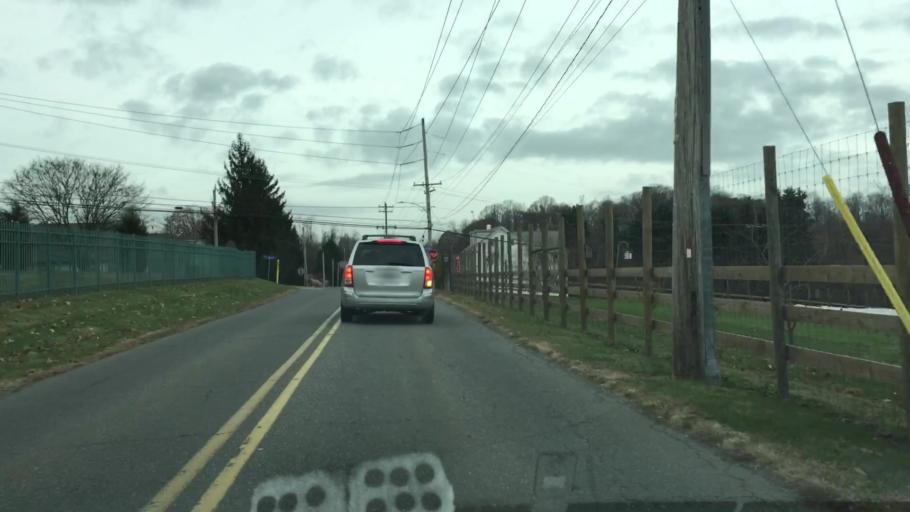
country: US
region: Pennsylvania
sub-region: Delaware County
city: Village Green-Green Ridge
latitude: 39.8738
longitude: -75.4350
